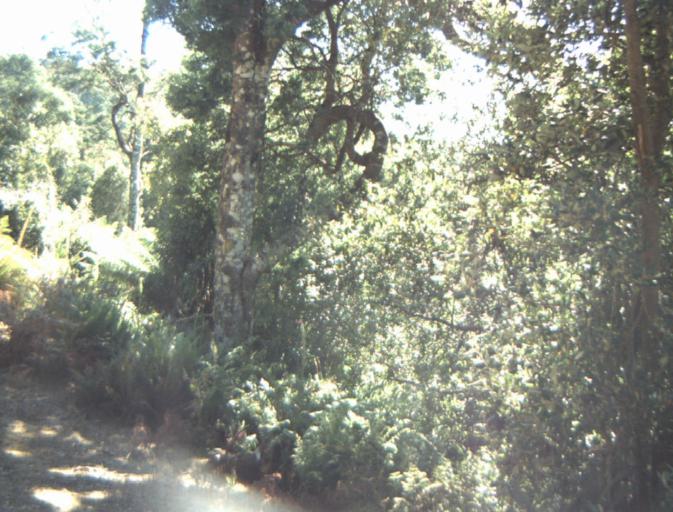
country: AU
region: Tasmania
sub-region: Dorset
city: Scottsdale
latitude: -41.2750
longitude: 147.3626
